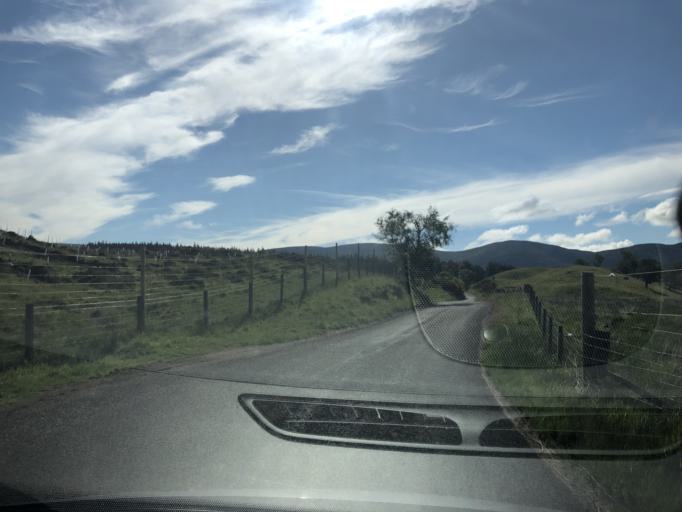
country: GB
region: Scotland
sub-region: Angus
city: Kirriemuir
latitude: 56.8321
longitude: -3.0687
